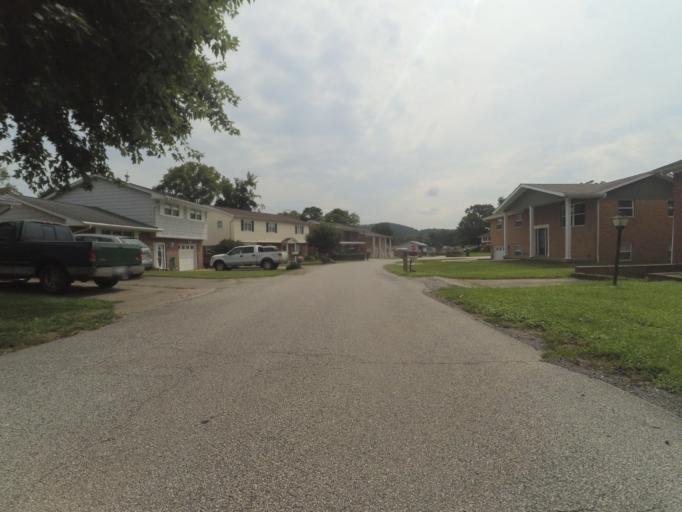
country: US
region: West Virginia
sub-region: Cabell County
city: Huntington
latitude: 38.4352
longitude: -82.4675
